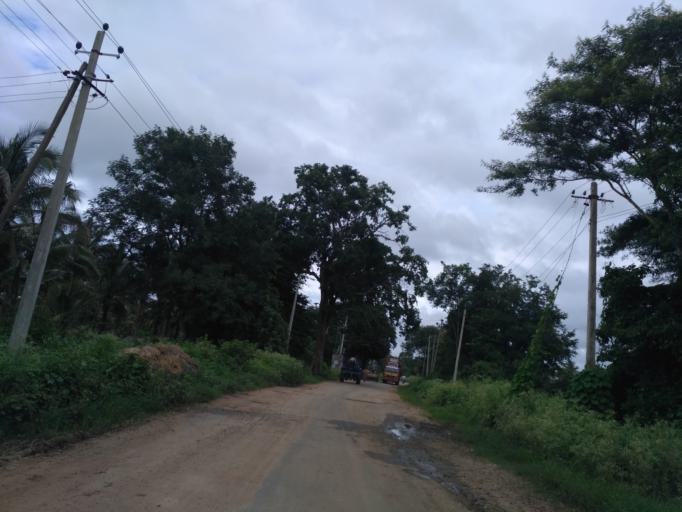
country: IN
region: Karnataka
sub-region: Hassan
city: Gorur
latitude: 12.8235
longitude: 76.0852
